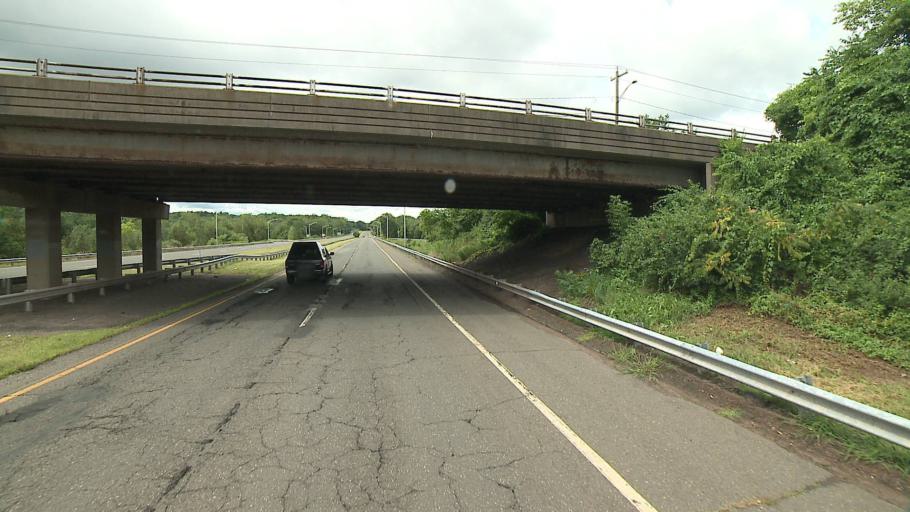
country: US
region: Connecticut
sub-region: Hartford County
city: Kensington
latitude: 41.6467
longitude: -72.7708
